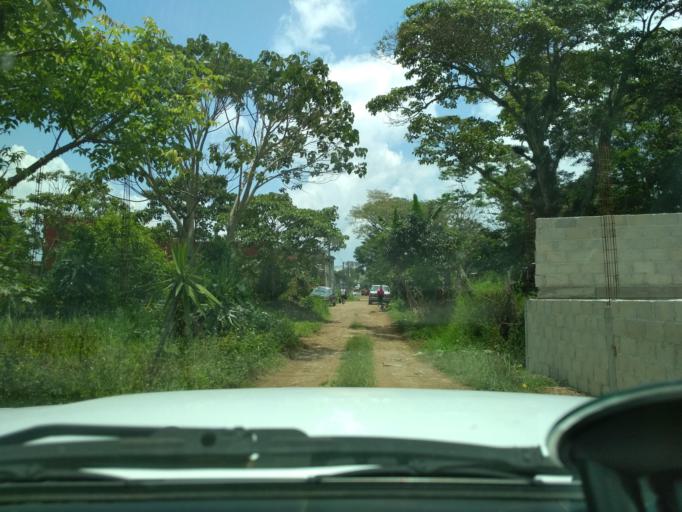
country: MX
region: Veracruz
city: Tocuila
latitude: 18.9501
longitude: -97.0189
